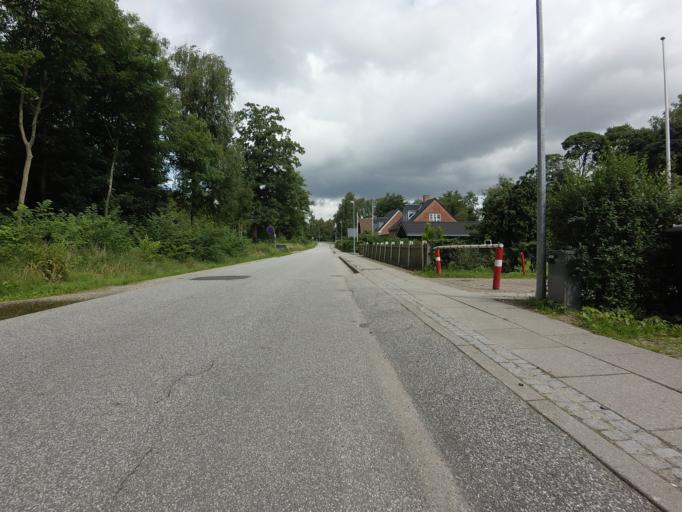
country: DK
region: Central Jutland
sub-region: Randers Kommune
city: Langa
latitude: 56.3897
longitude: 9.9015
